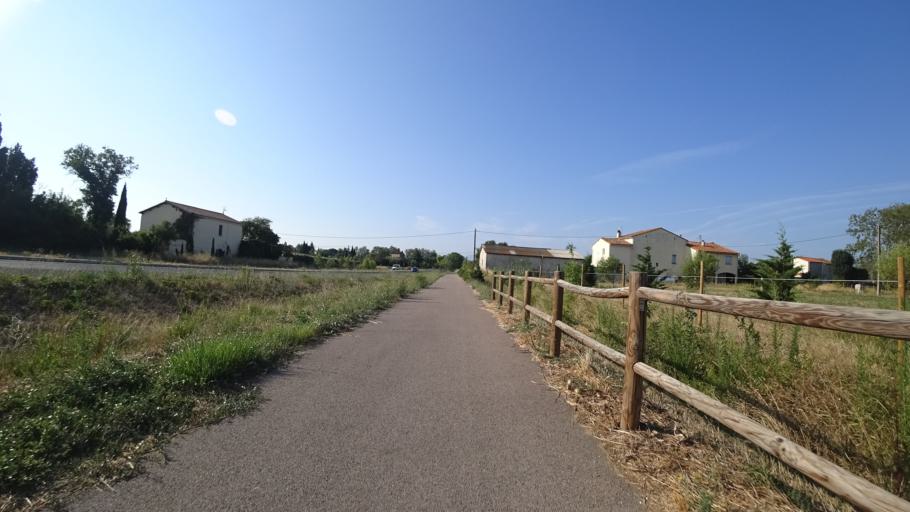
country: FR
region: Languedoc-Roussillon
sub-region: Departement des Pyrenees-Orientales
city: Perpignan
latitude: 42.7205
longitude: 2.9030
